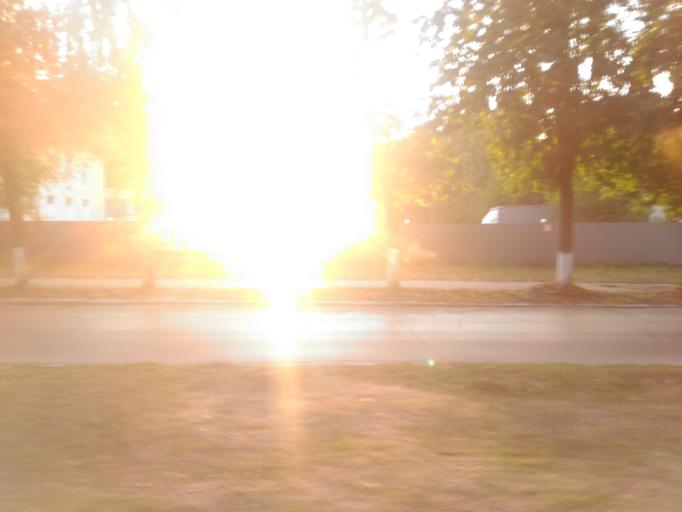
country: RU
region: Ulyanovsk
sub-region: Ulyanovskiy Rayon
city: Ulyanovsk
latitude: 54.3059
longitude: 48.3231
